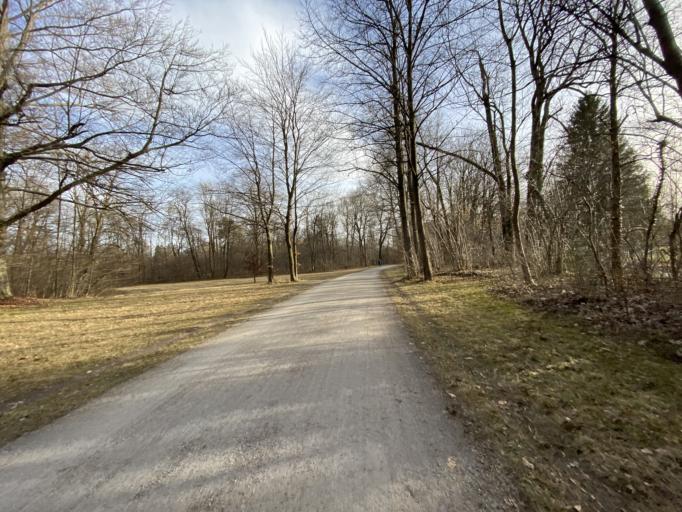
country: DE
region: Bavaria
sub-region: Upper Bavaria
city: Bogenhausen
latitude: 48.1763
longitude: 11.6104
